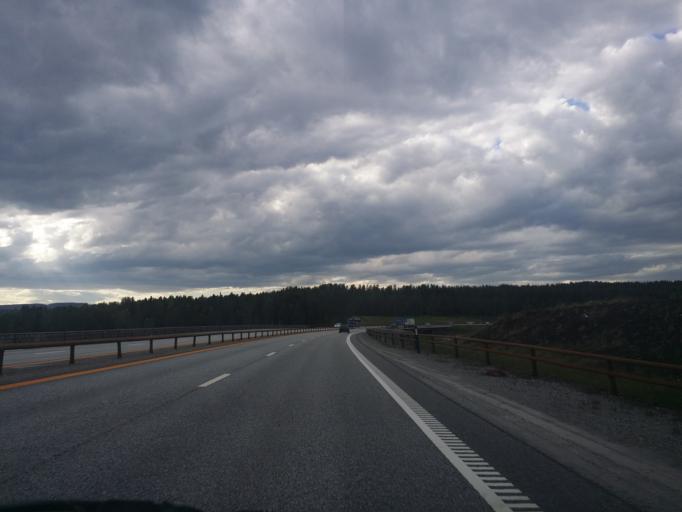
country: NO
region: Akershus
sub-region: Eidsvoll
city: Raholt
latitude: 60.2836
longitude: 11.1390
